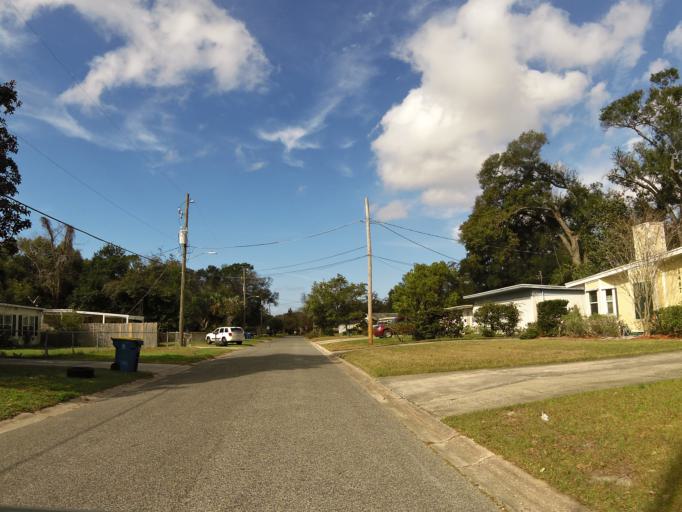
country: US
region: Florida
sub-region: Duval County
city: Jacksonville
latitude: 30.3390
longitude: -81.5834
